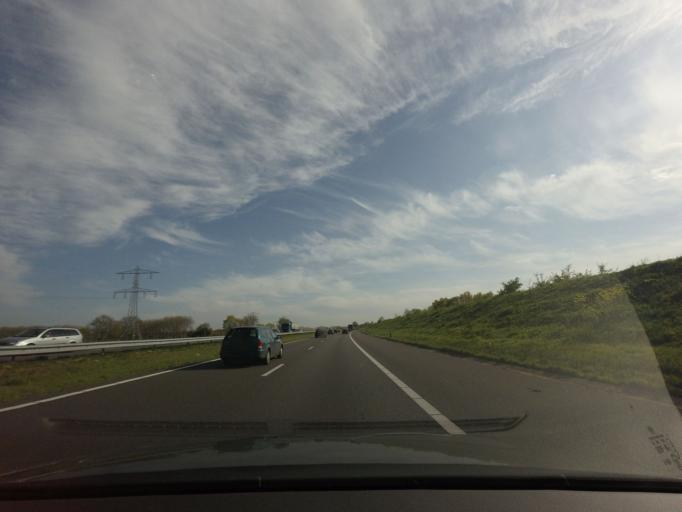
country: NL
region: North Brabant
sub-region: Gemeente Uden
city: Uden
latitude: 51.6978
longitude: 5.5765
